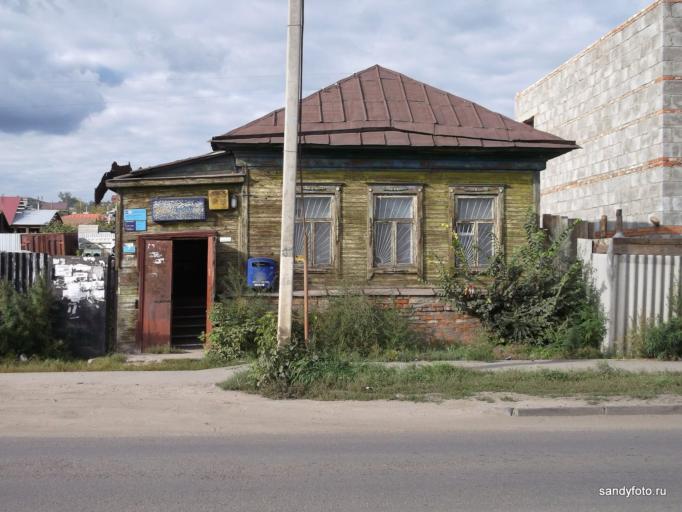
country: RU
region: Chelyabinsk
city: Troitsk
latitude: 54.0948
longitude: 61.5708
